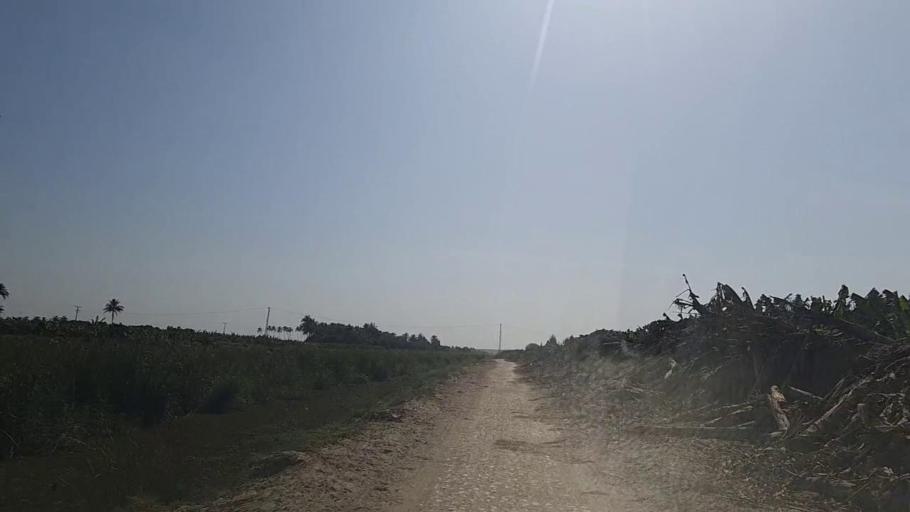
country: PK
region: Sindh
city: Thatta
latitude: 24.6394
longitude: 67.8888
